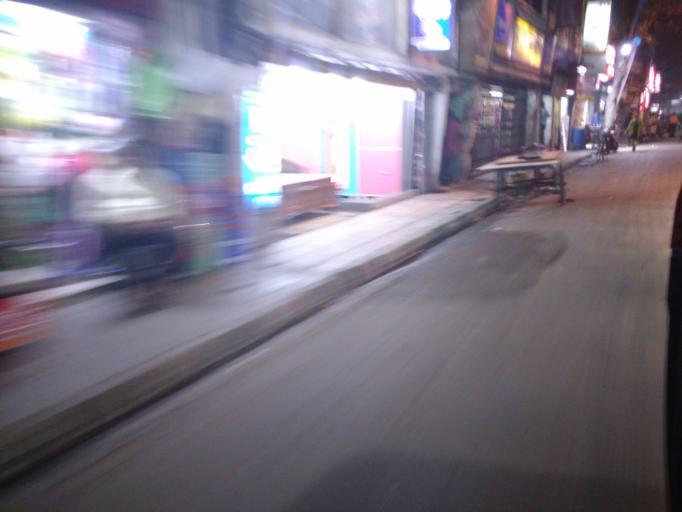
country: IN
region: West Bengal
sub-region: North 24 Parganas
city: Baranagar
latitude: 22.6326
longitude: 88.3715
